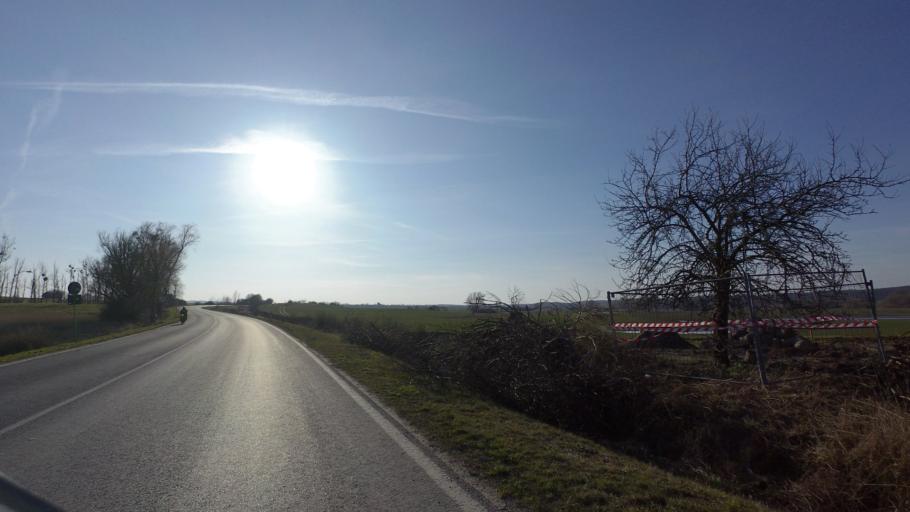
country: DE
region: Brandenburg
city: Chorin
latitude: 52.9588
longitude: 13.9246
